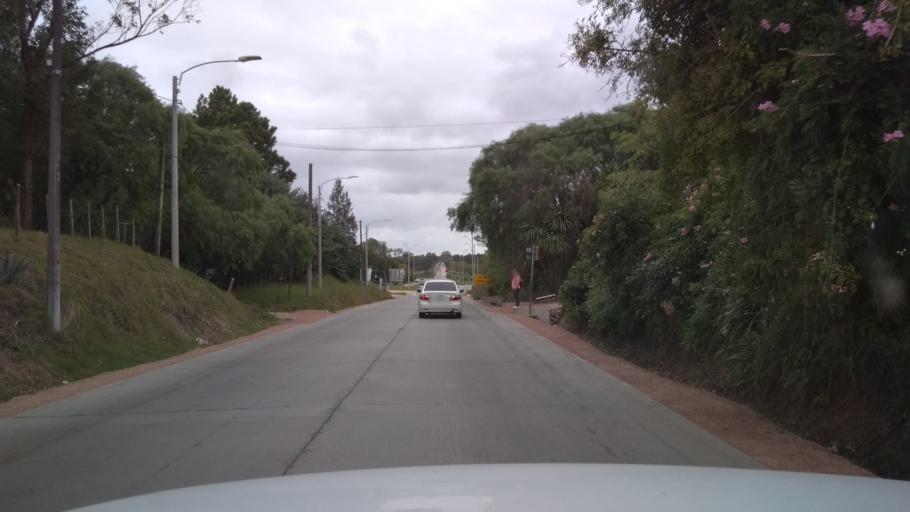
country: UY
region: Canelones
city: Toledo
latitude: -34.7951
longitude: -56.1505
